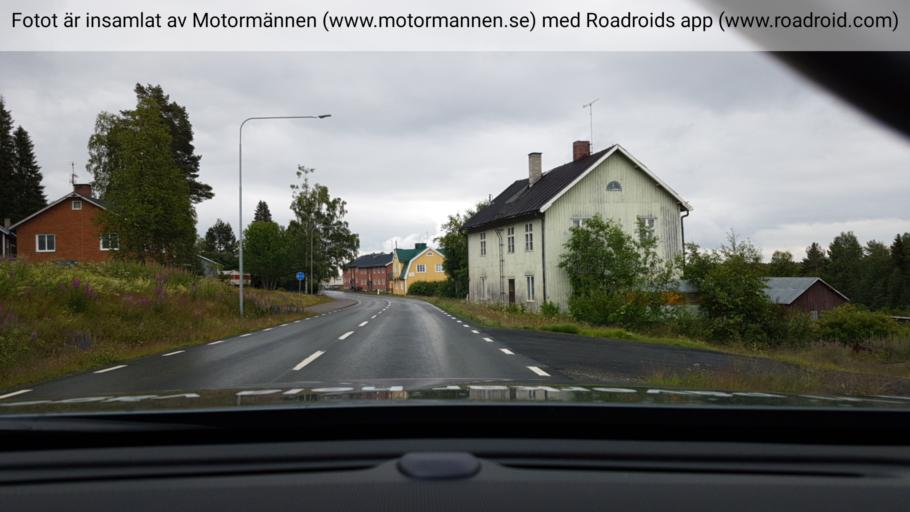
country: SE
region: Vaesterbotten
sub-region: Norsjo Kommun
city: Norsjoe
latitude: 65.2629
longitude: 19.6194
